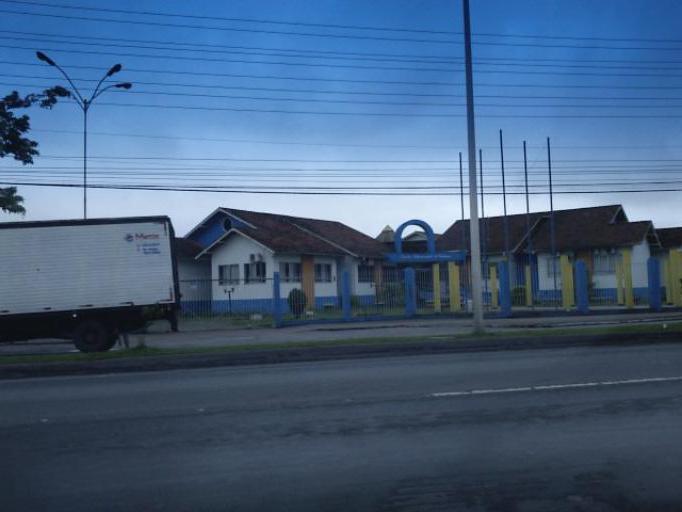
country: BR
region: Santa Catarina
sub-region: Itajai
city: Itajai
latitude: -26.8880
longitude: -48.7015
